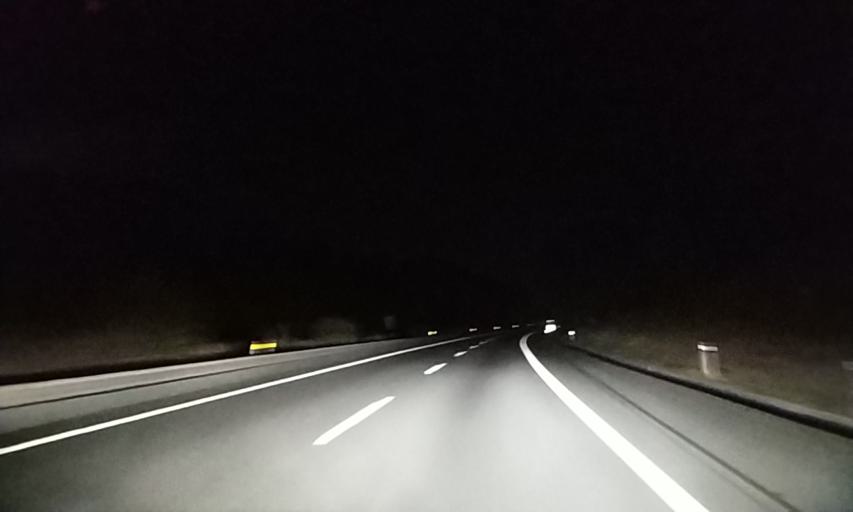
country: PT
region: Aveiro
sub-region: Albergaria-A-Velha
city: Albergaria-a-Velha
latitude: 40.6766
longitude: -8.5195
